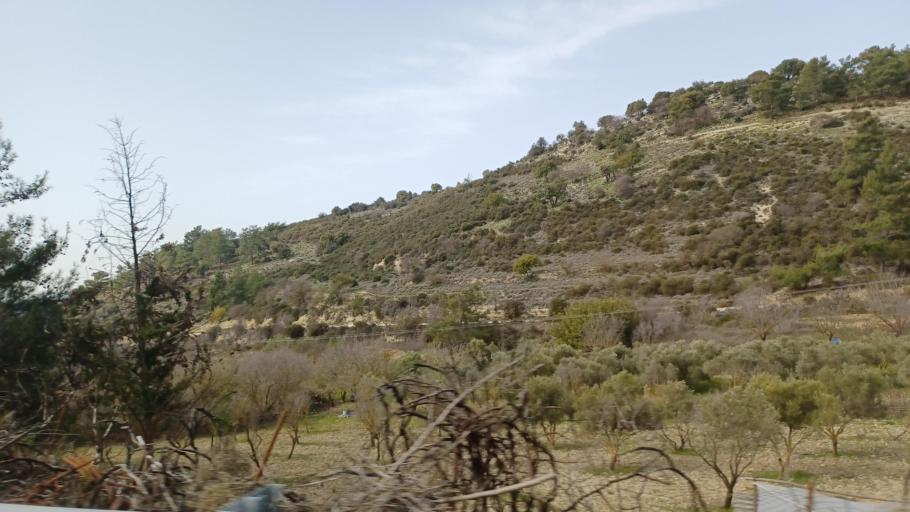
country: CY
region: Limassol
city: Pachna
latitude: 34.7658
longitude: 32.7024
